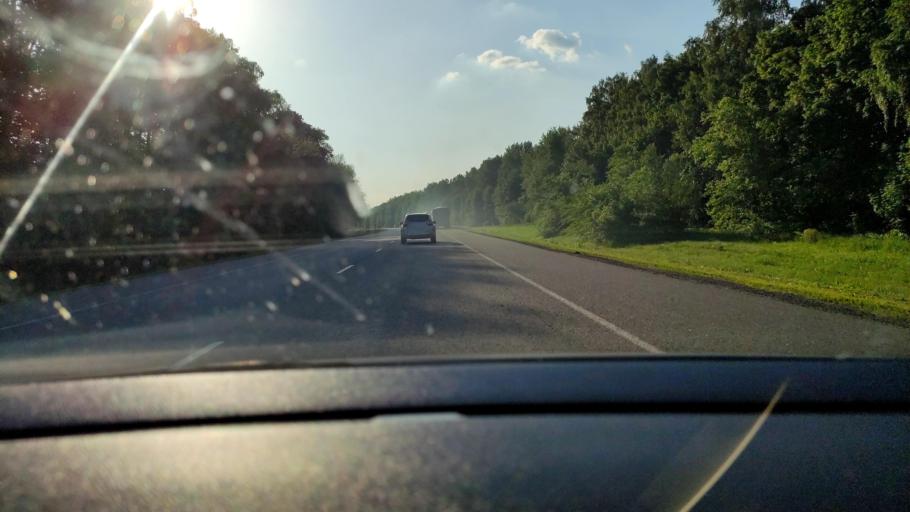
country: RU
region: Voronezj
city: Kashirskoye
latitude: 51.4856
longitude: 39.6505
